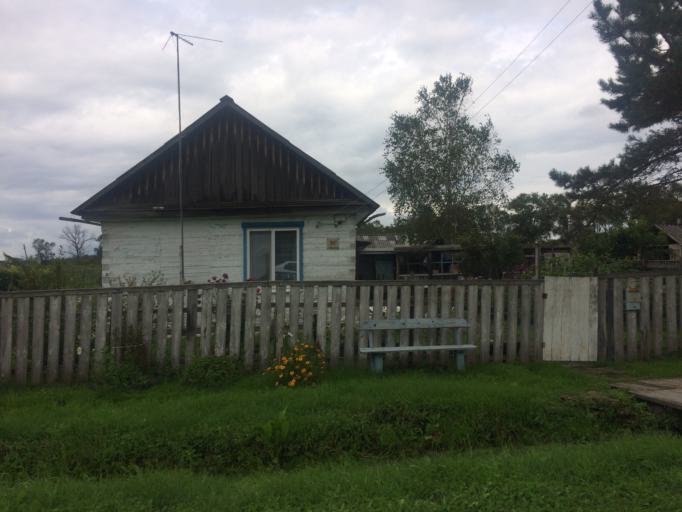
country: RU
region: Primorskiy
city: Lazo
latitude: 45.8301
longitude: 133.6141
